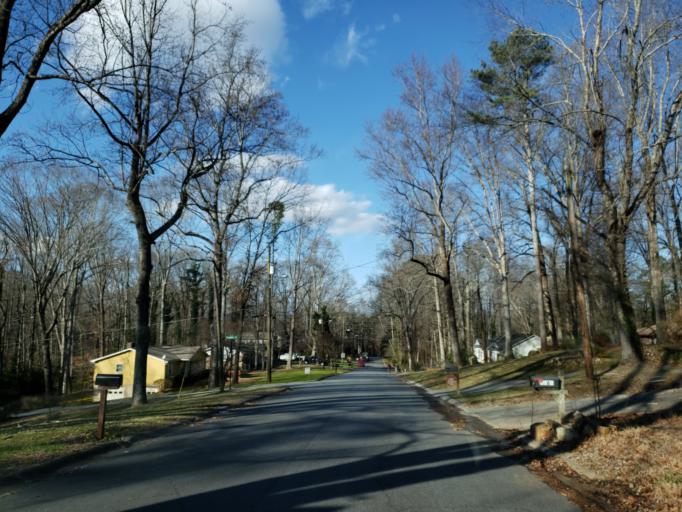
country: US
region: Georgia
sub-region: Cherokee County
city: Woodstock
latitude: 34.0323
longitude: -84.4872
